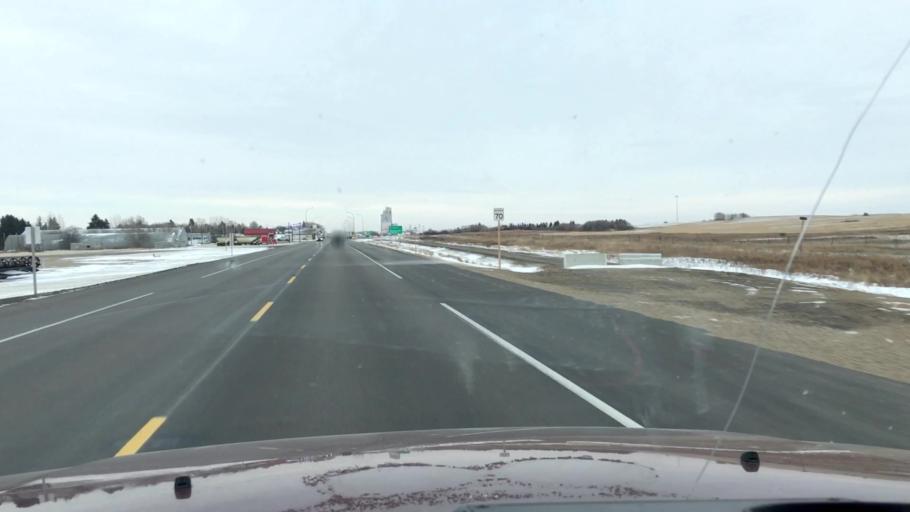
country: CA
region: Saskatchewan
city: Moose Jaw
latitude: 50.8550
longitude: -105.5761
